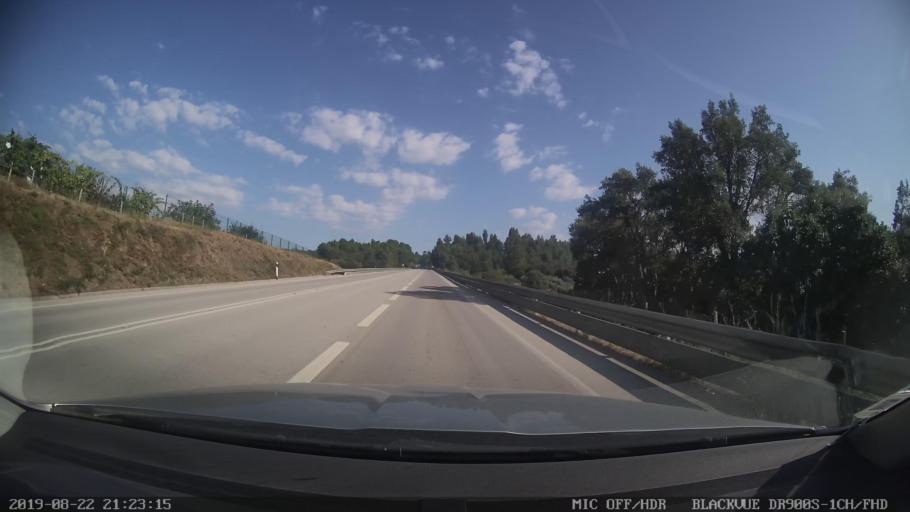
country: PT
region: Castelo Branco
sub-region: Serta
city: Serta
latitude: 39.8283
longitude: -8.1081
